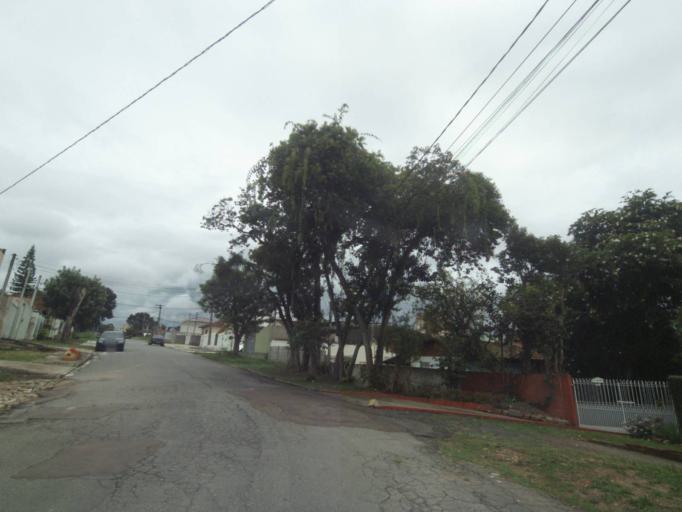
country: BR
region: Parana
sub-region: Curitiba
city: Curitiba
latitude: -25.4865
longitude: -49.2895
